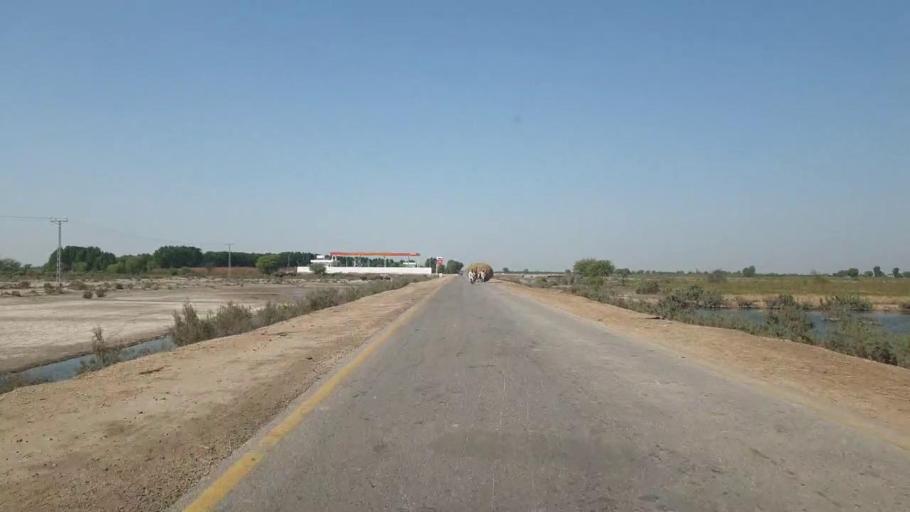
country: PK
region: Sindh
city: Rajo Khanani
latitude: 25.0050
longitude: 68.8373
